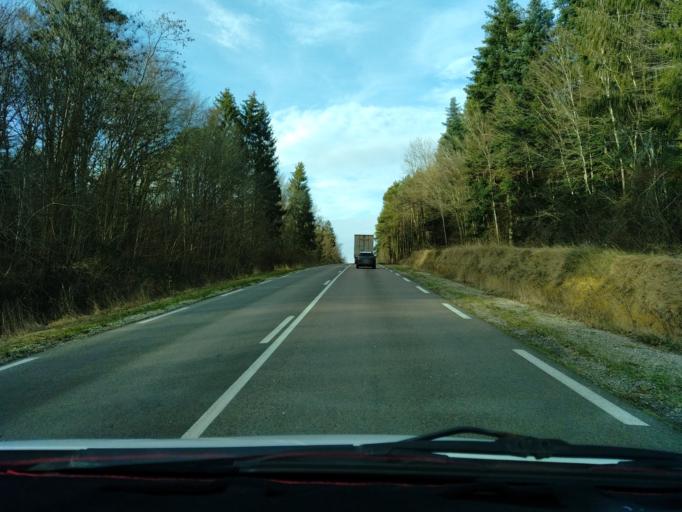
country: FR
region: Franche-Comte
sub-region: Departement de la Haute-Saone
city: Gray
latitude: 47.4011
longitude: 5.6434
